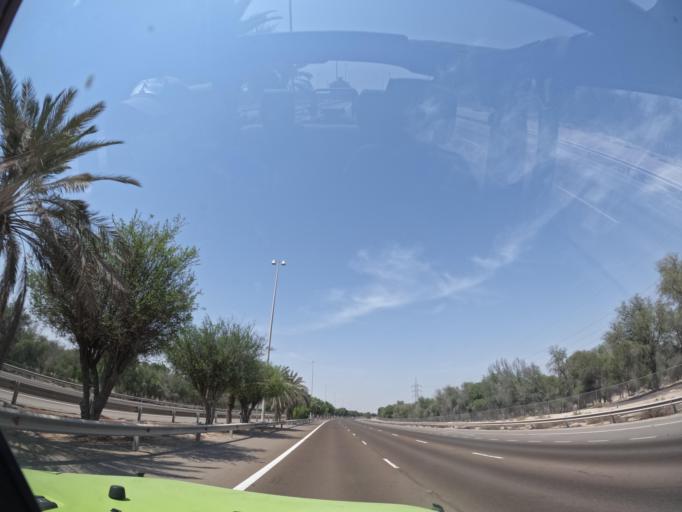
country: AE
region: Abu Dhabi
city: Abu Dhabi
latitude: 24.2415
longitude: 54.7324
